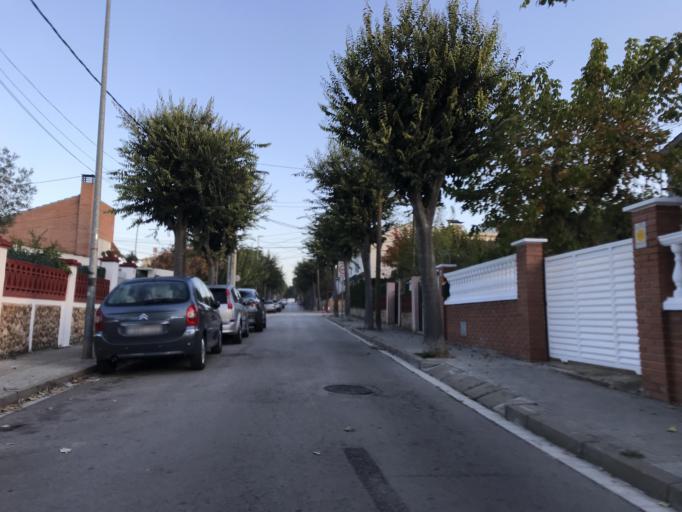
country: ES
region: Catalonia
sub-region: Provincia de Barcelona
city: Parets del Valles
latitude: 41.5596
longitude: 2.2218
